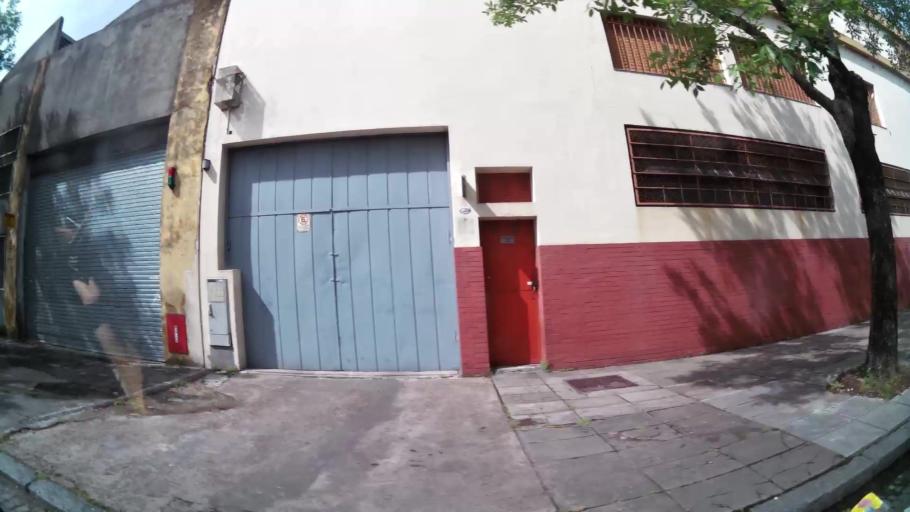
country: AR
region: Buenos Aires F.D.
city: Villa Lugano
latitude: -34.6511
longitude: -58.4307
